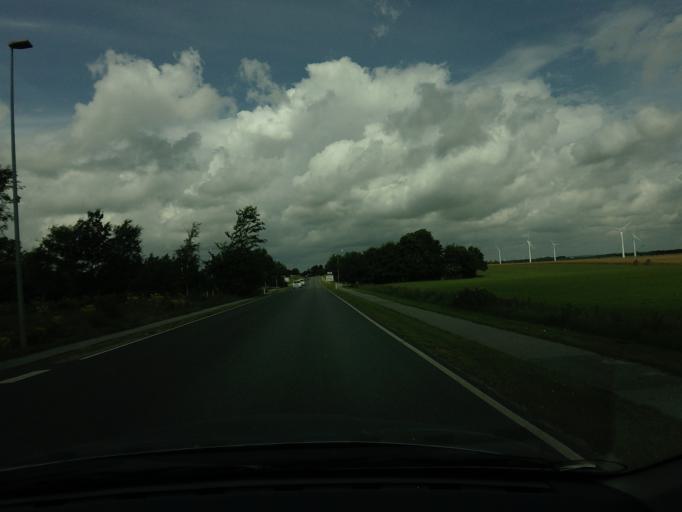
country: DK
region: North Denmark
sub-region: Hjorring Kommune
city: Tars
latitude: 57.3900
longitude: 10.1057
